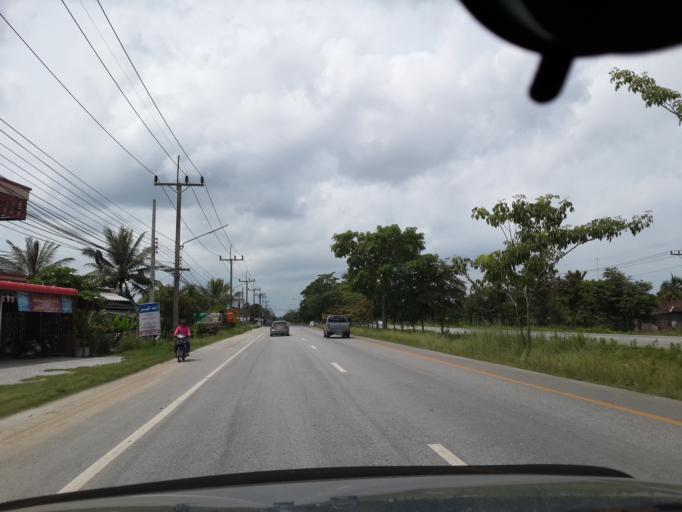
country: TH
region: Pattani
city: Yaring
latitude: 6.8676
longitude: 101.3376
